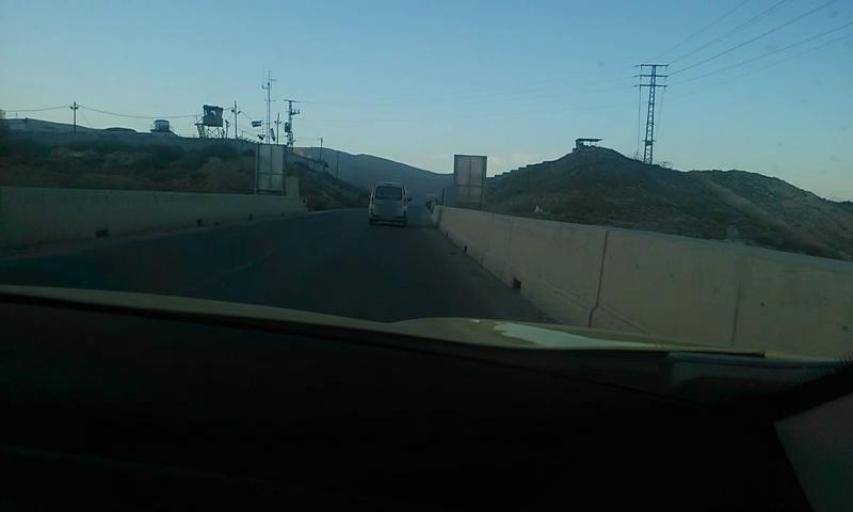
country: PS
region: West Bank
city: An Nuway`imah
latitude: 31.9108
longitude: 35.4222
